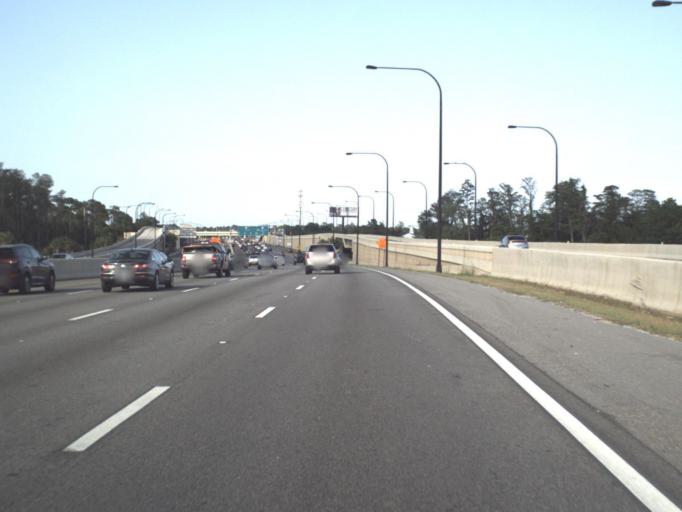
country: US
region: Florida
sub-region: Orange County
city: Azalea Park
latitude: 28.5407
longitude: -81.2852
